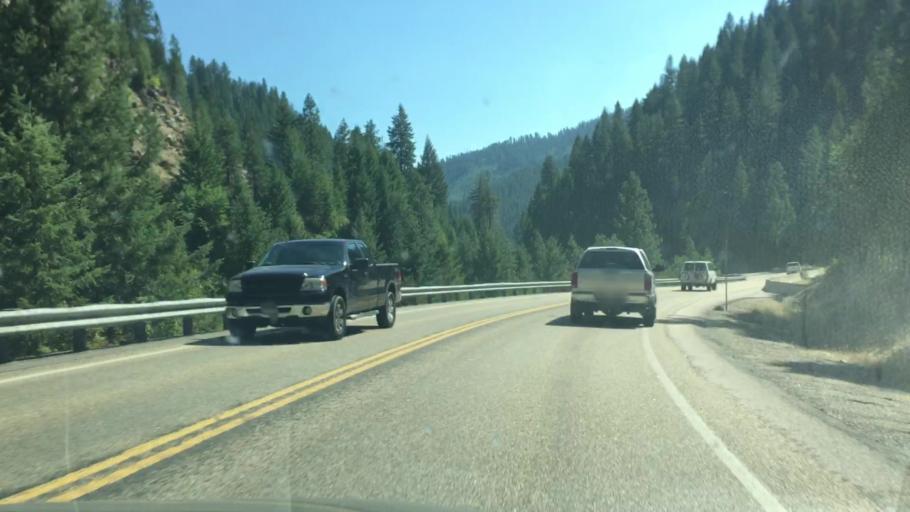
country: US
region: Idaho
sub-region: Valley County
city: Cascade
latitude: 44.1487
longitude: -116.1120
